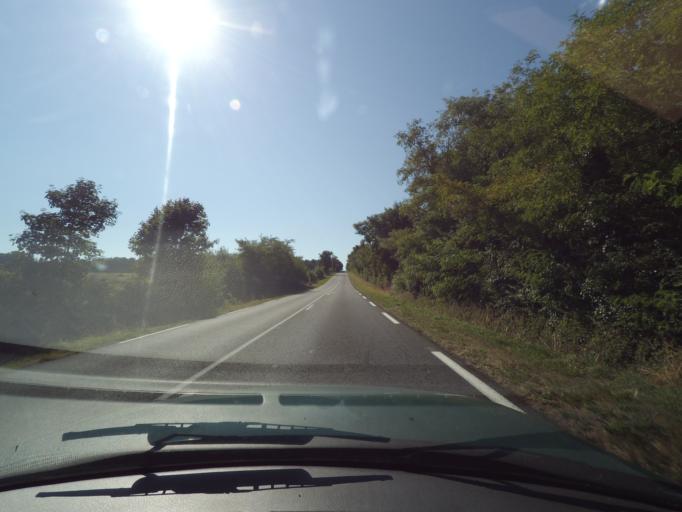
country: FR
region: Poitou-Charentes
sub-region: Departement de la Vienne
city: Lussac-les-Chateaux
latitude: 46.3593
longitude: 0.7773
